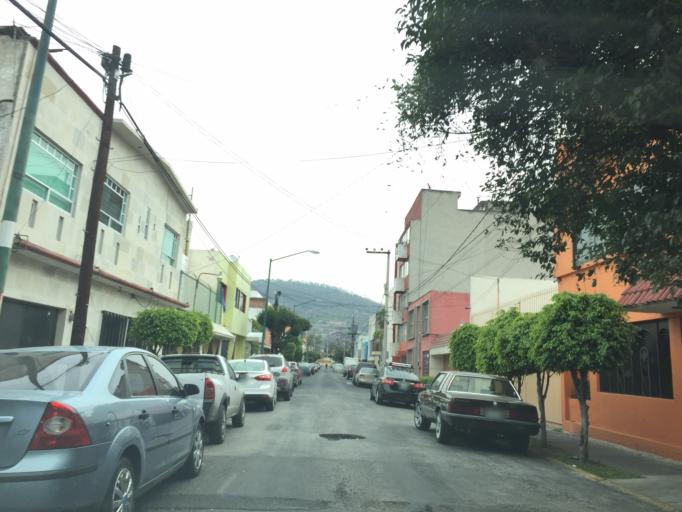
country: MX
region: Mexico
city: Colonia Lindavista
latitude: 19.4952
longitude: -99.1253
